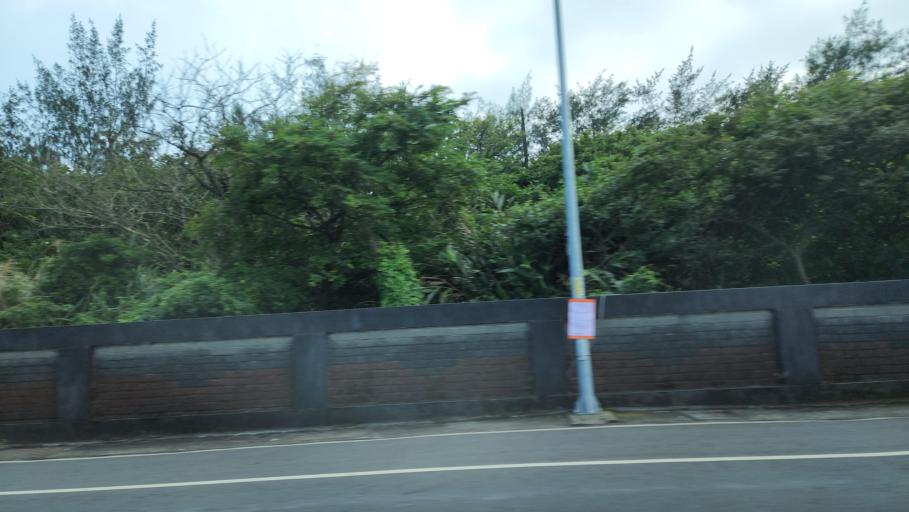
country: TW
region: Taiwan
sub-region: Keelung
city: Keelung
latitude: 25.2281
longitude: 121.6410
